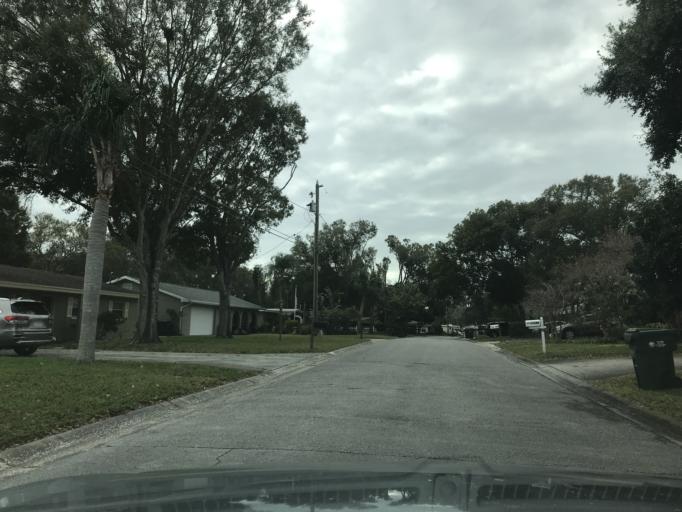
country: US
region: Florida
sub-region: Pinellas County
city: Largo
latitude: 27.9344
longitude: -82.7796
